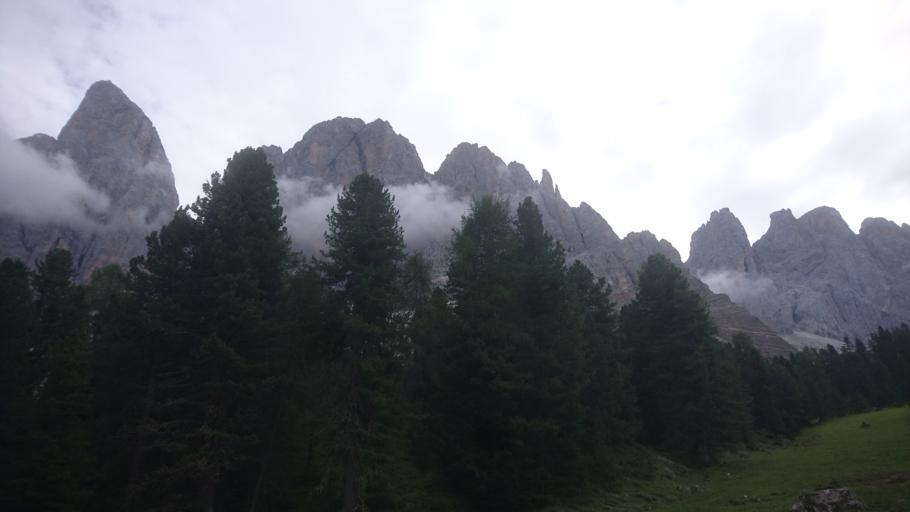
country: IT
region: Trentino-Alto Adige
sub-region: Bolzano
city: Santa Cristina Valgardena
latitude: 46.6185
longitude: 11.7580
